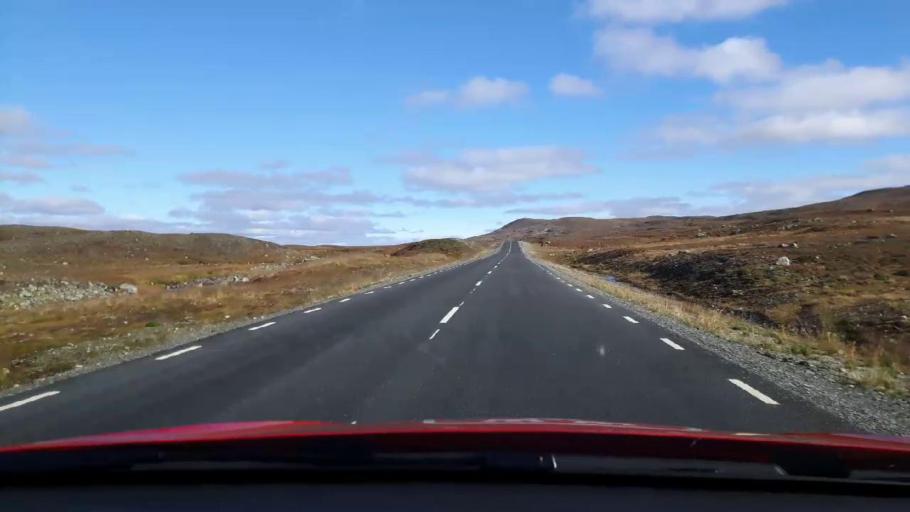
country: NO
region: Nordland
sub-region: Hattfjelldal
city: Hattfjelldal
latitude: 65.0557
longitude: 14.3569
